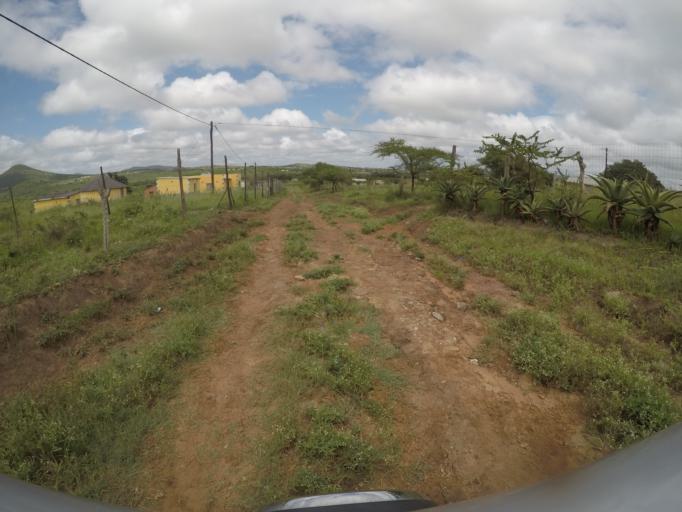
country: ZA
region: KwaZulu-Natal
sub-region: uThungulu District Municipality
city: Empangeni
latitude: -28.5834
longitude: 31.8492
